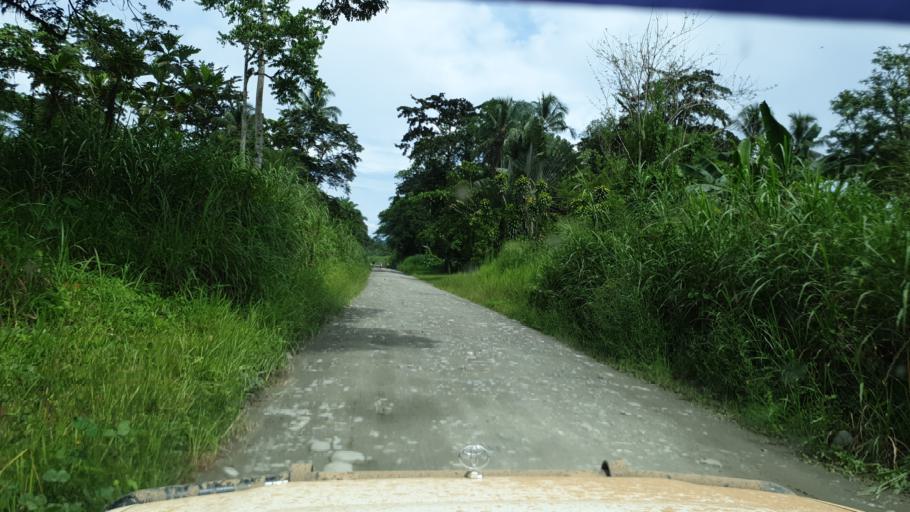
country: PG
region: Northern Province
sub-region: Sohe
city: Kokoda
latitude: -8.8946
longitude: 147.7499
